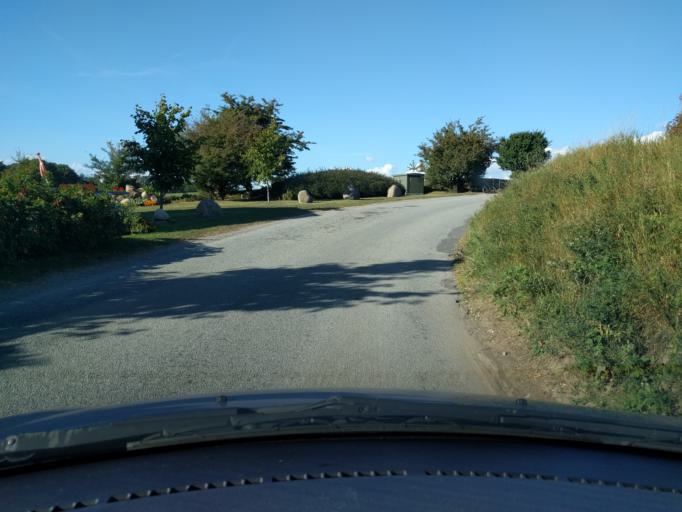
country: DK
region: South Denmark
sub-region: Assens Kommune
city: Harby
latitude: 55.1355
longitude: 10.0262
